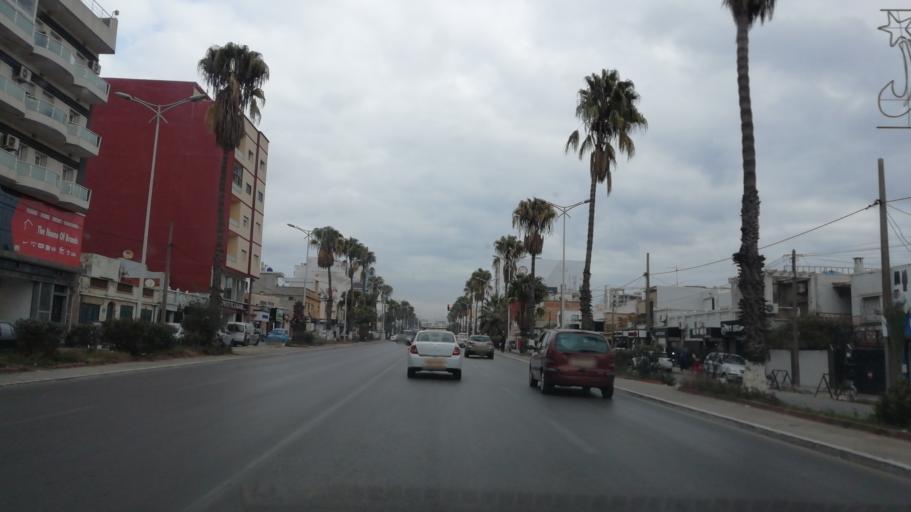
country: DZ
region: Oran
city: Oran
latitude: 35.6937
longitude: -0.6170
